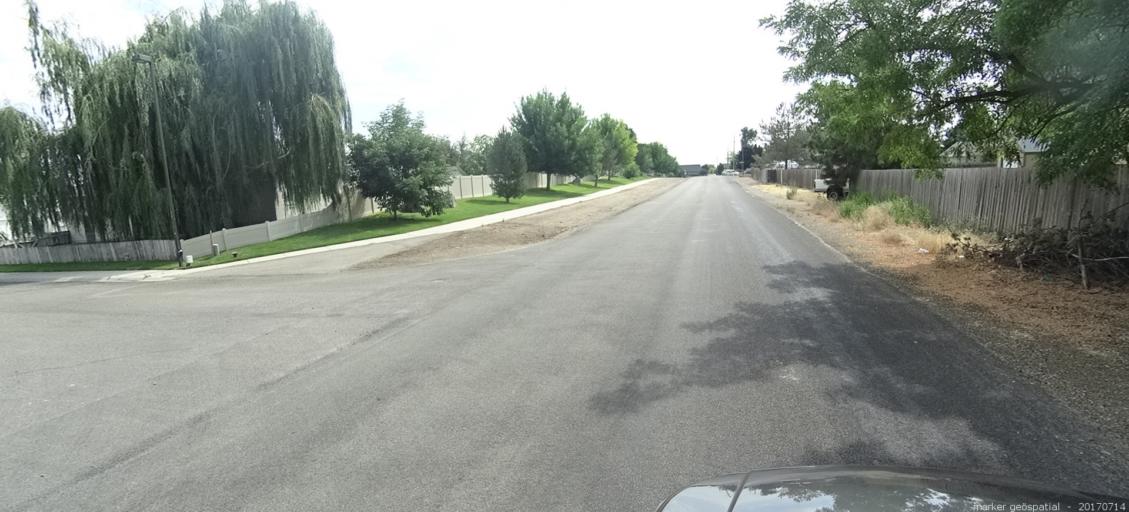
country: US
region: Idaho
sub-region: Ada County
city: Kuna
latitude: 43.4921
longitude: -116.4074
